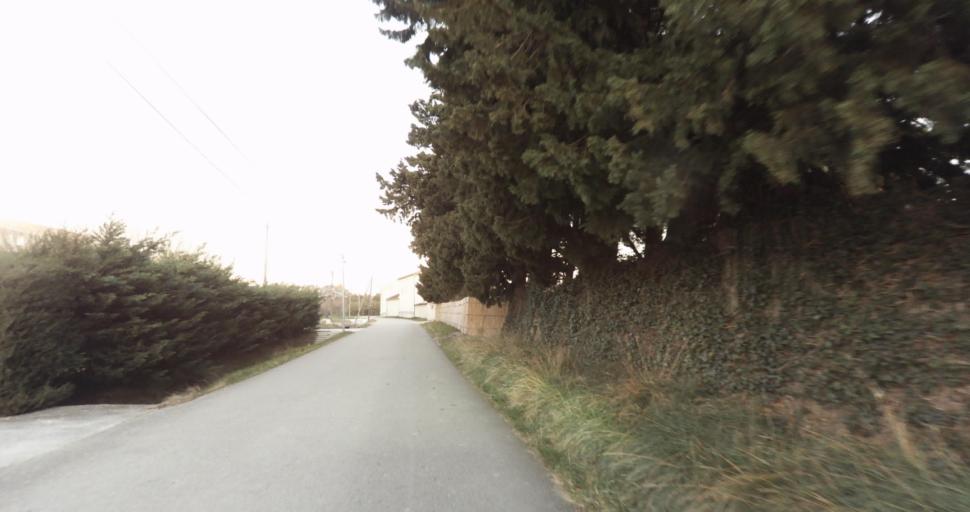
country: FR
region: Provence-Alpes-Cote d'Azur
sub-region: Departement des Bouches-du-Rhone
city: Barbentane
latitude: 43.9106
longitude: 4.7672
